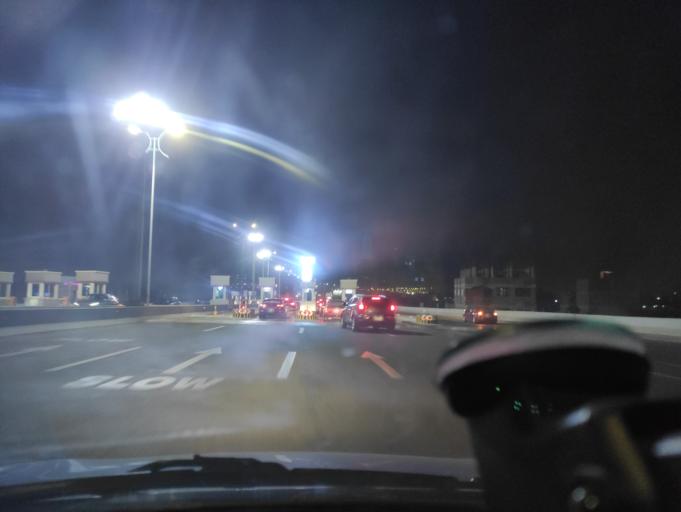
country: EG
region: Muhafazat al Qahirah
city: Cairo
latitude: 30.1115
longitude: 31.2237
